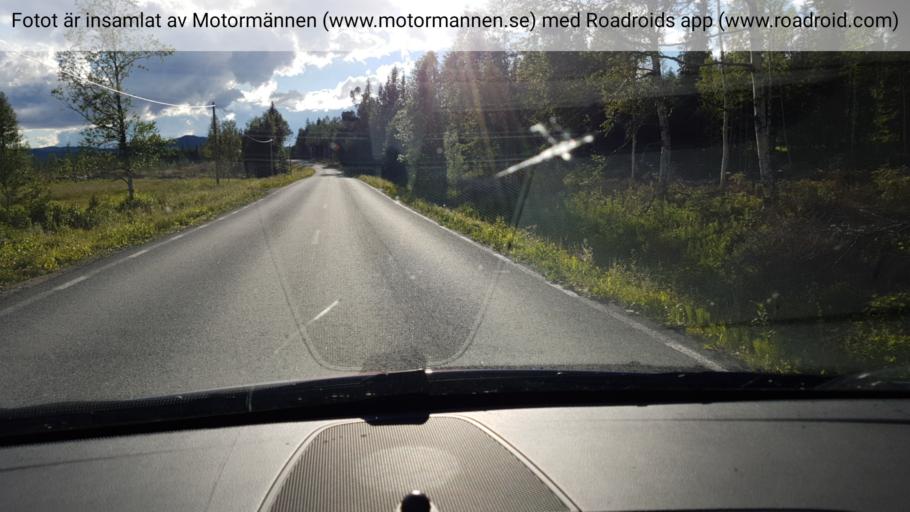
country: SE
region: Jaemtland
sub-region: Are Kommun
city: Are
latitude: 63.3141
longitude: 13.1627
